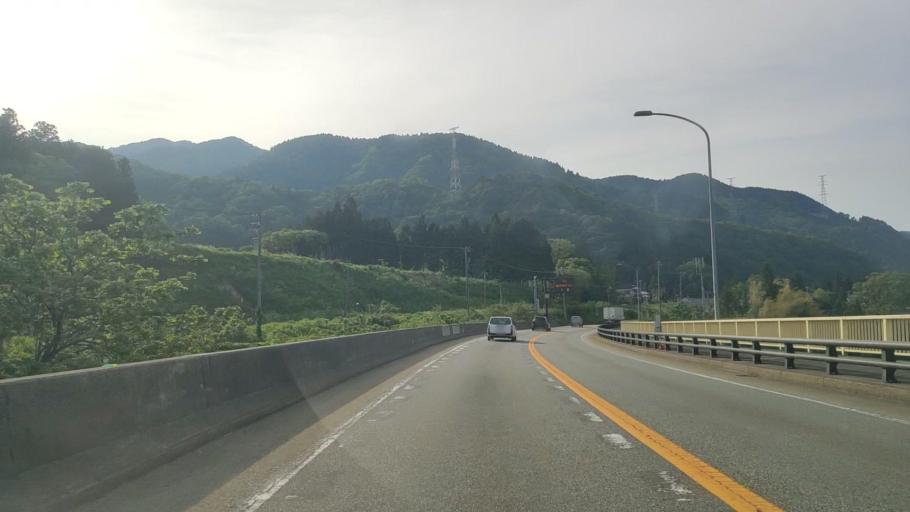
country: JP
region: Toyama
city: Yatsuomachi-higashikumisaka
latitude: 36.5057
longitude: 137.2311
